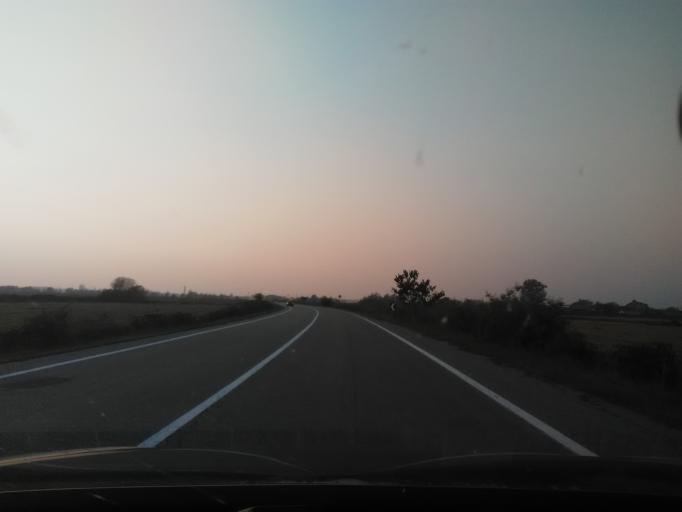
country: IT
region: Piedmont
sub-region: Provincia di Vercelli
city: Prarolo
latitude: 45.2954
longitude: 8.4456
